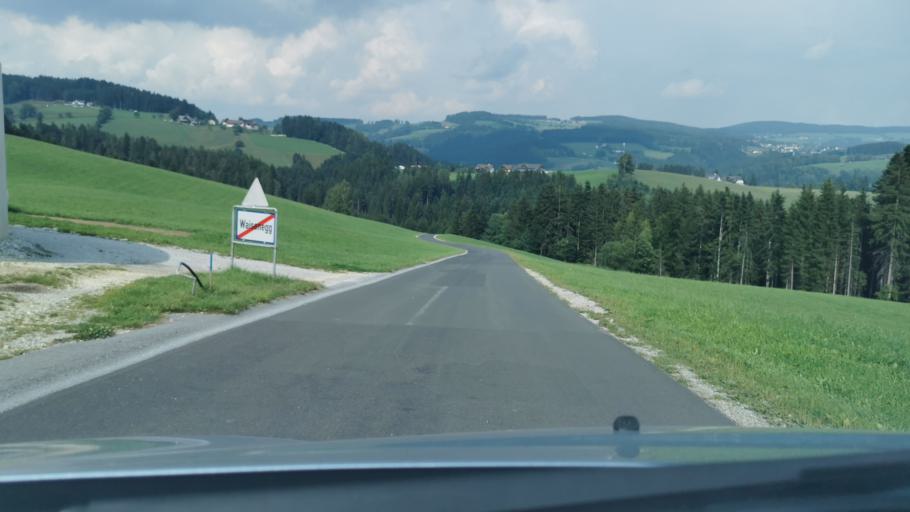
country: AT
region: Styria
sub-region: Politischer Bezirk Weiz
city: Strallegg
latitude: 47.3957
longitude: 15.6838
